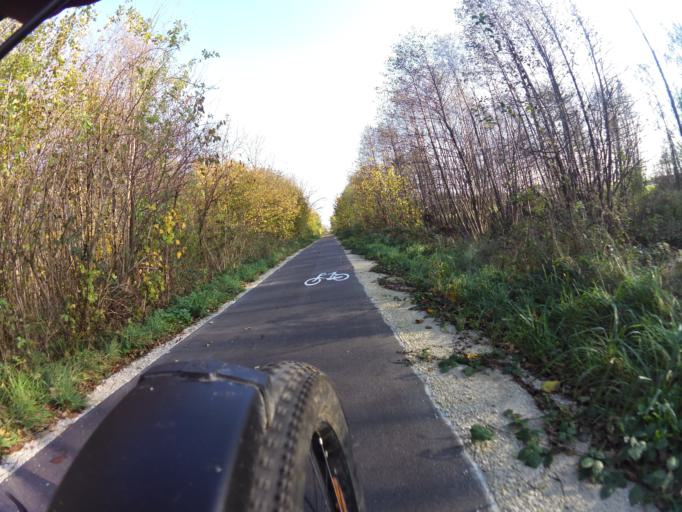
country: PL
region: Pomeranian Voivodeship
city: Strzelno
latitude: 54.7633
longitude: 18.2623
